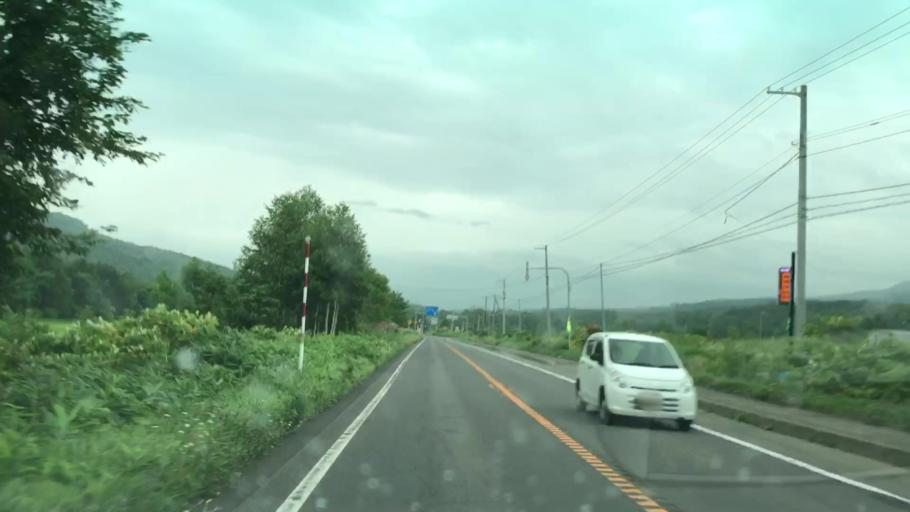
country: JP
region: Hokkaido
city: Niseko Town
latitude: 42.7678
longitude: 140.4849
